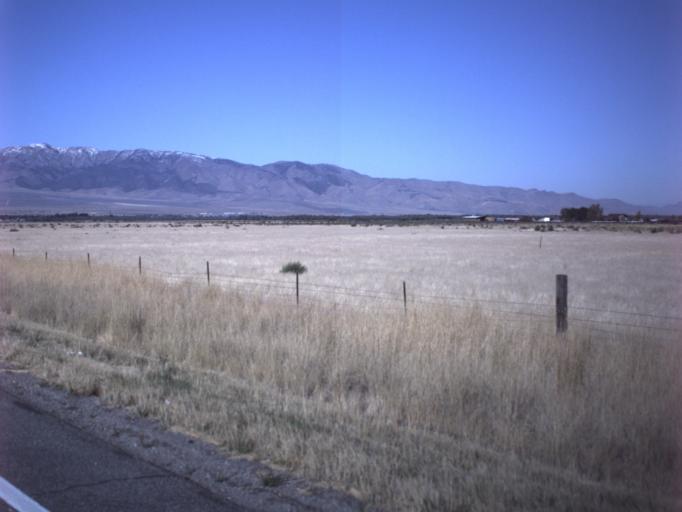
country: US
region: Utah
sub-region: Tooele County
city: Grantsville
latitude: 40.6036
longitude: -112.3966
